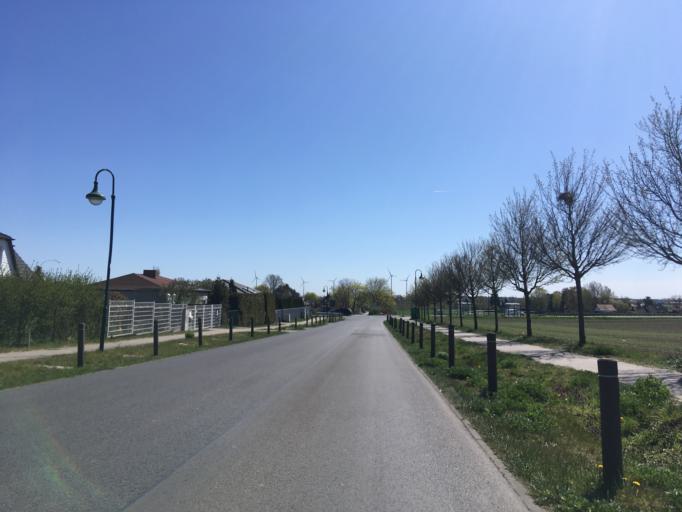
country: DE
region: Brandenburg
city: Bernau bei Berlin
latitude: 52.6418
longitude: 13.5607
